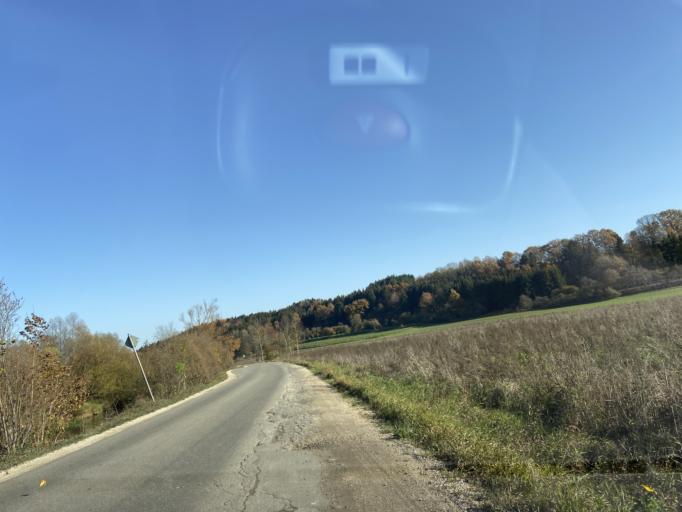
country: DE
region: Baden-Wuerttemberg
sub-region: Tuebingen Region
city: Krauchenwies
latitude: 48.0297
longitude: 9.2505
